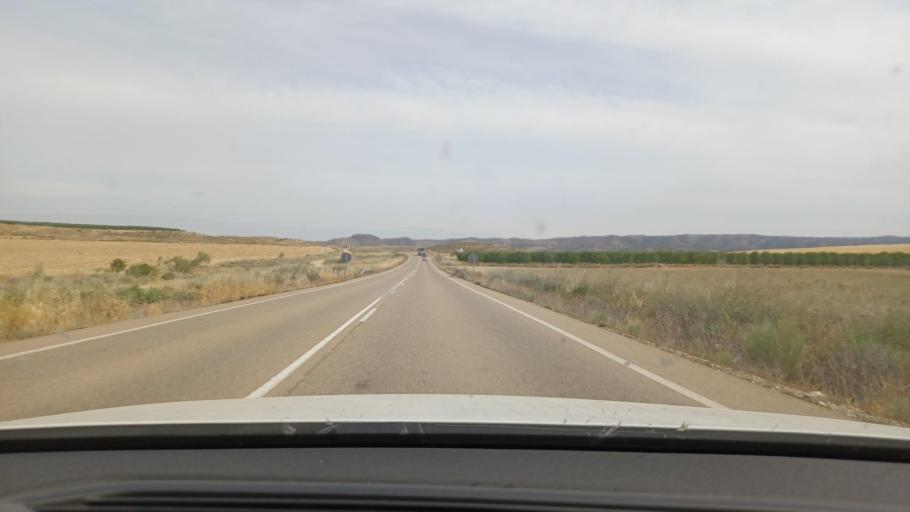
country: ES
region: Aragon
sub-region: Provincia de Zaragoza
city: Chiprana
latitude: 41.2999
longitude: -0.0686
